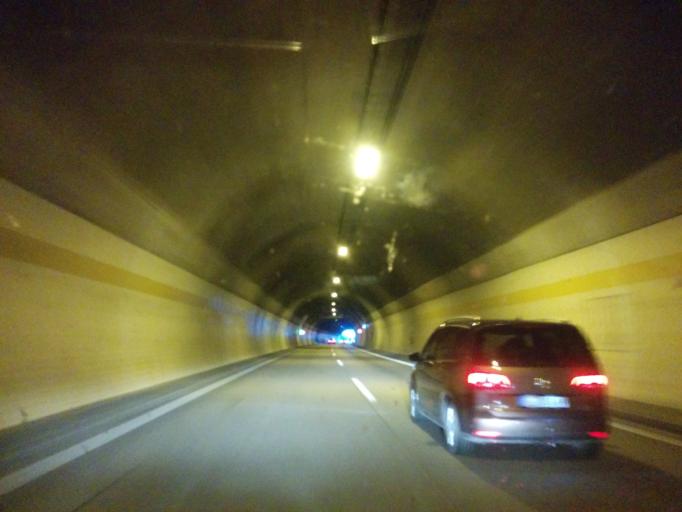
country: DE
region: Baden-Wuerttemberg
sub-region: Regierungsbezirk Stuttgart
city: Ellenberg
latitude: 49.0214
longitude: 10.1967
